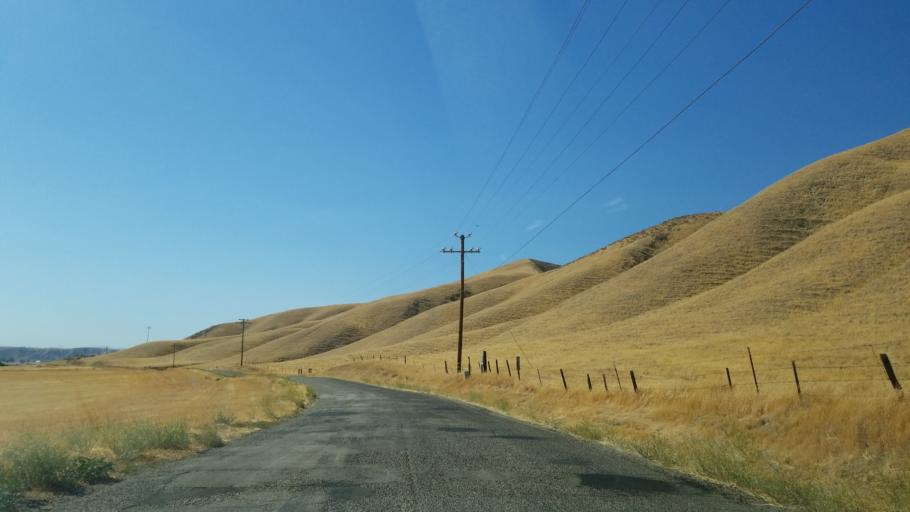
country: US
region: California
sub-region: San Luis Obispo County
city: San Miguel
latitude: 35.7859
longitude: -120.7085
